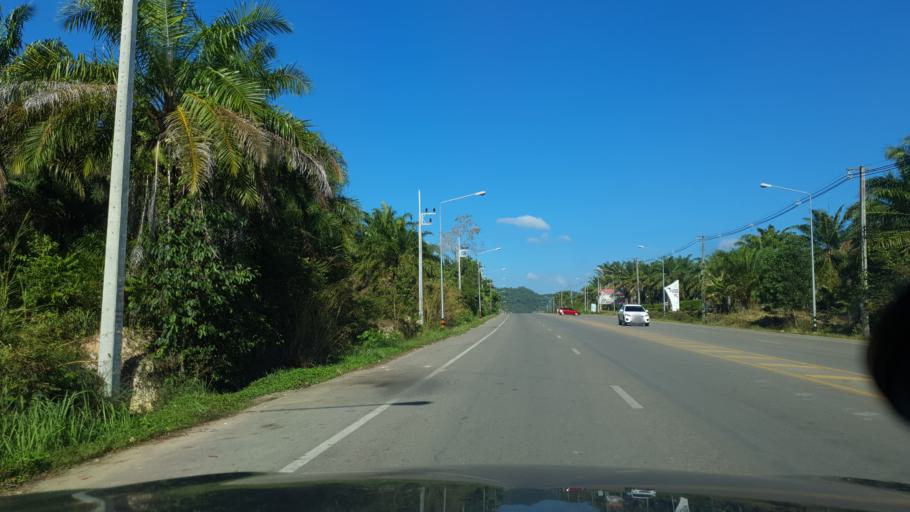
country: TH
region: Phangnga
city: Ban Ao Nang
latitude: 8.0366
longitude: 98.8554
